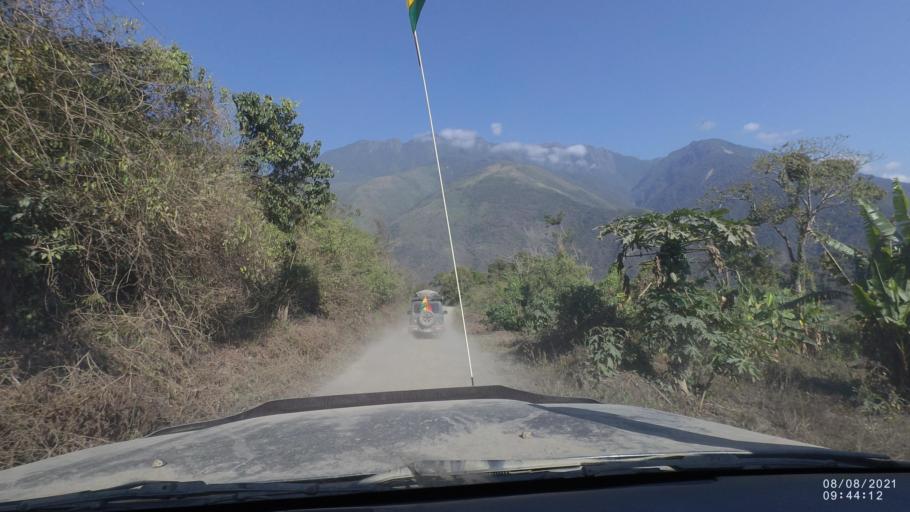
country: BO
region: La Paz
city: Quime
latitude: -16.6012
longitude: -66.7221
